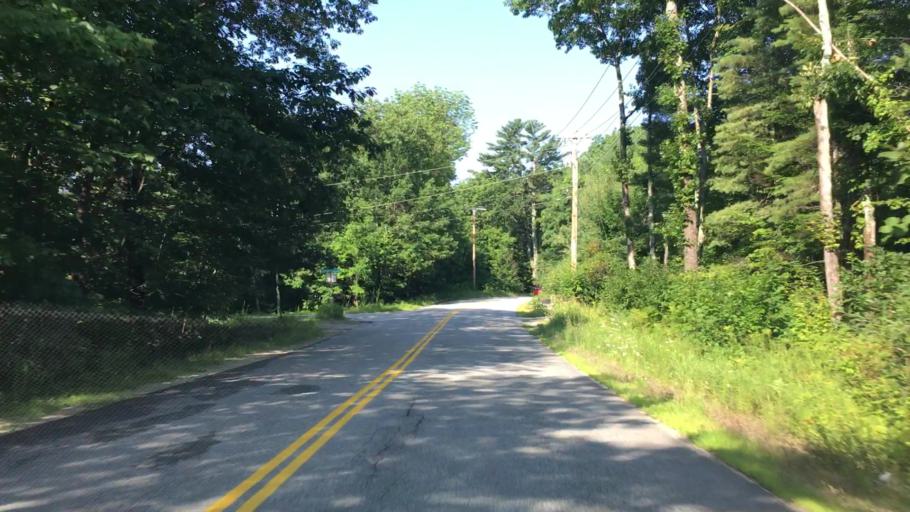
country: US
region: Maine
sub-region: Androscoggin County
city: Minot
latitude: 44.0432
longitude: -70.3158
